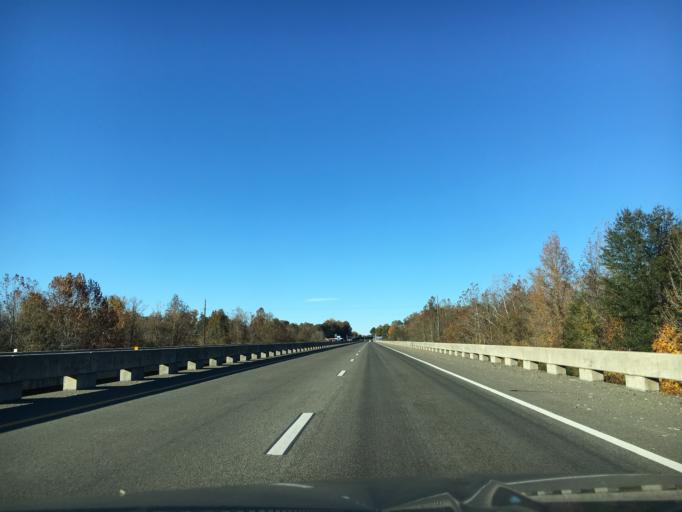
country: US
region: Virginia
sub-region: Halifax County
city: South Boston
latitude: 36.6917
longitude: -78.8874
